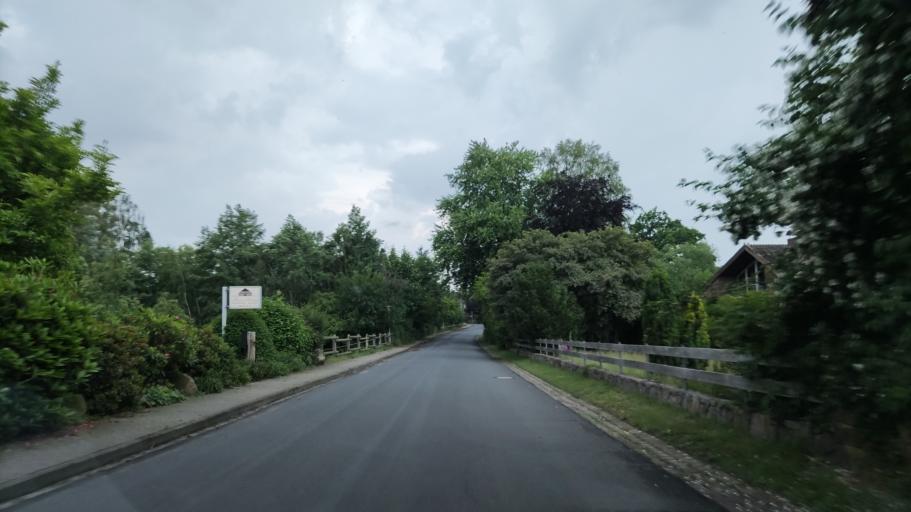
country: DE
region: Lower Saxony
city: Rullstorf
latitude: 53.2876
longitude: 10.5314
